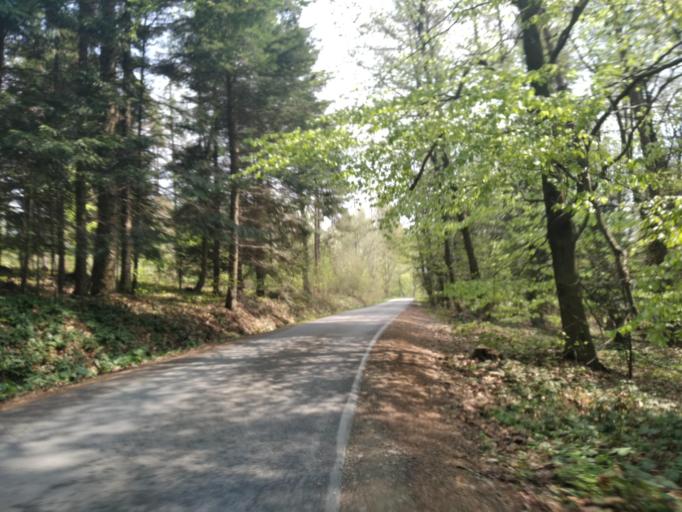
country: PL
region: Subcarpathian Voivodeship
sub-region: Powiat krosnienski
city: Iwonicz-Zdroj
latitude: 49.5427
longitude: 21.7926
